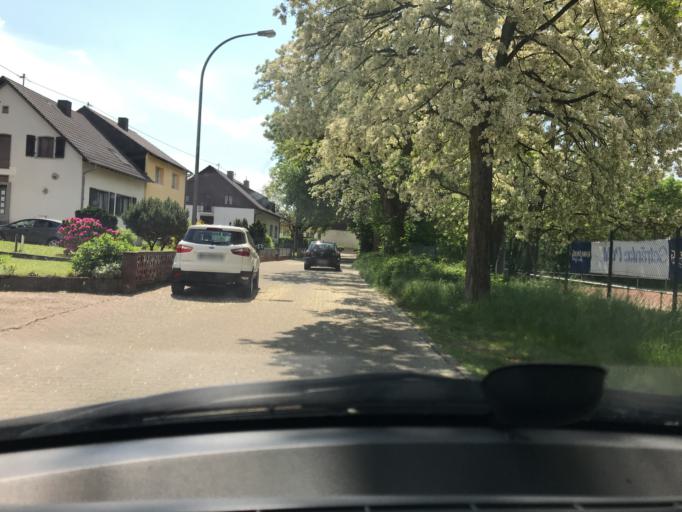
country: DE
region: Saarland
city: Saarlouis
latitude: 49.3334
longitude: 6.7598
